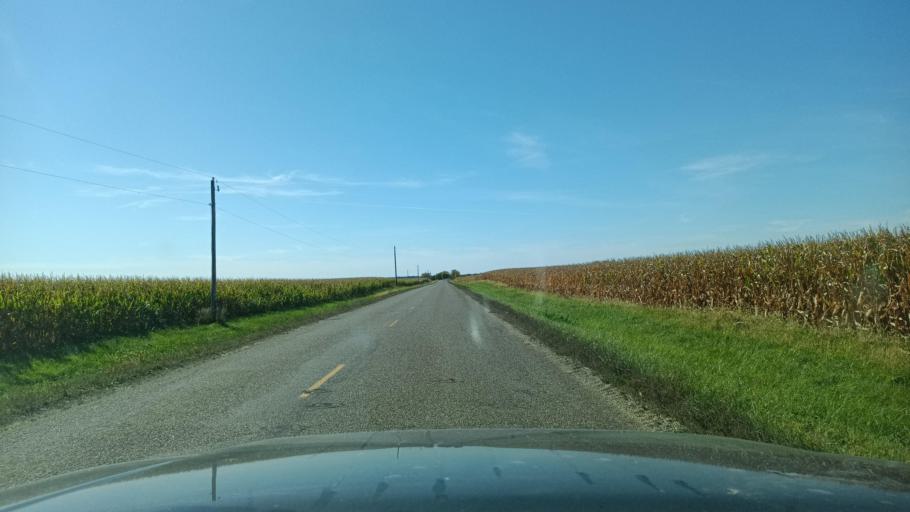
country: US
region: Illinois
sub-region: Logan County
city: Atlanta
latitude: 40.2344
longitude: -89.1412
